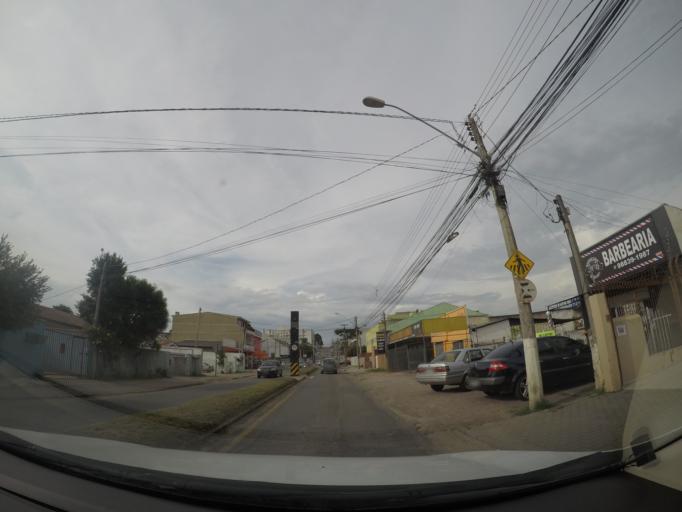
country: BR
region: Parana
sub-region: Sao Jose Dos Pinhais
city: Sao Jose dos Pinhais
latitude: -25.4911
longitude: -49.2291
